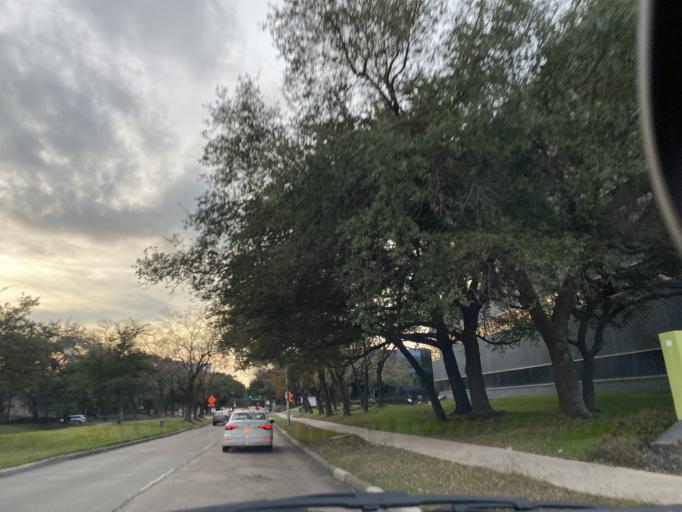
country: US
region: Texas
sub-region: Harris County
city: Bunker Hill Village
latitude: 29.7279
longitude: -95.5659
